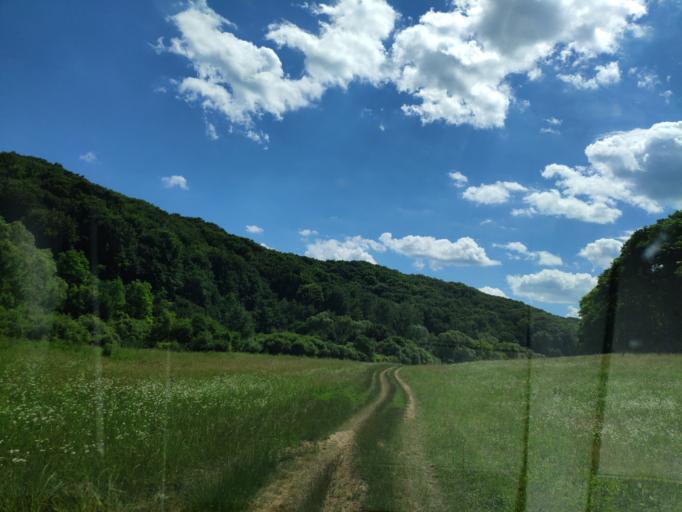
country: HU
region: Borsod-Abauj-Zemplen
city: Arlo
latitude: 48.2602
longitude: 20.1879
